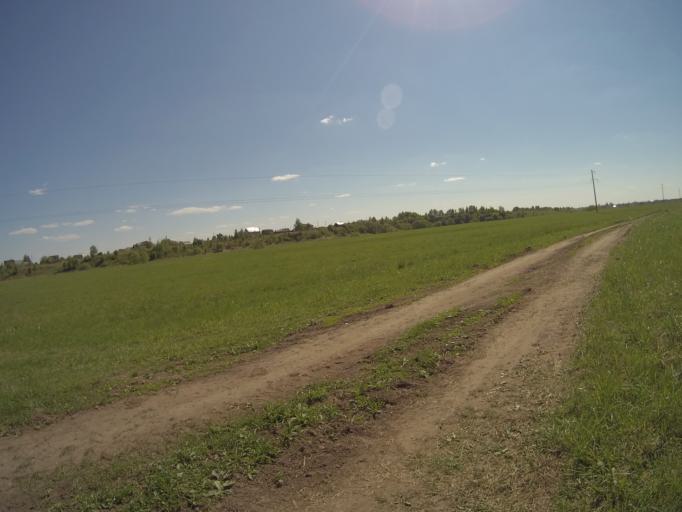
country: RU
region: Vladimir
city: Kideksha
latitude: 56.4218
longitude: 40.5279
